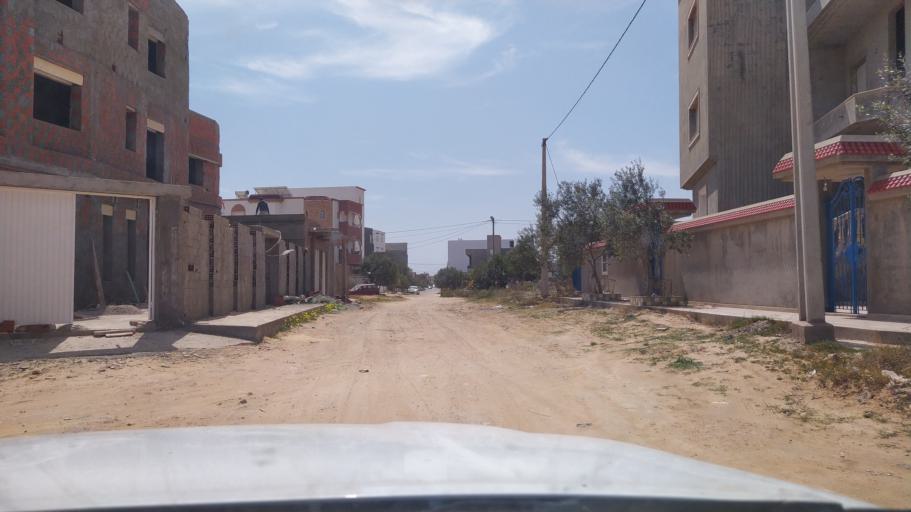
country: TN
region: Al Mahdiyah
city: Zouila
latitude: 35.5043
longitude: 11.0355
